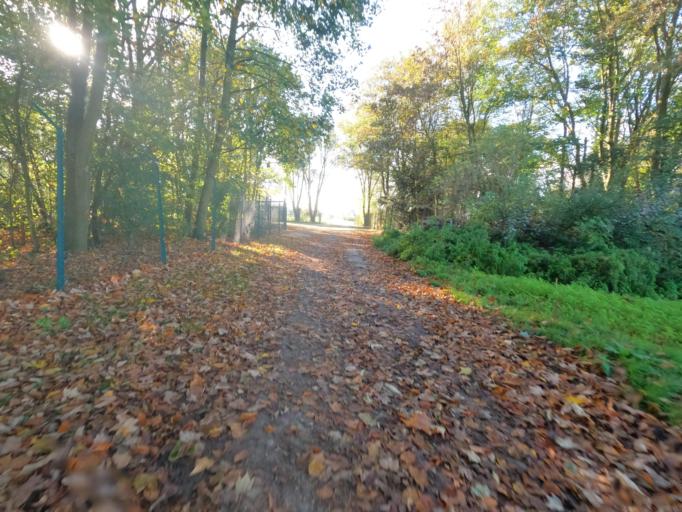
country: DE
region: North Rhine-Westphalia
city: Erkelenz
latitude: 51.0962
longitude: 6.3335
